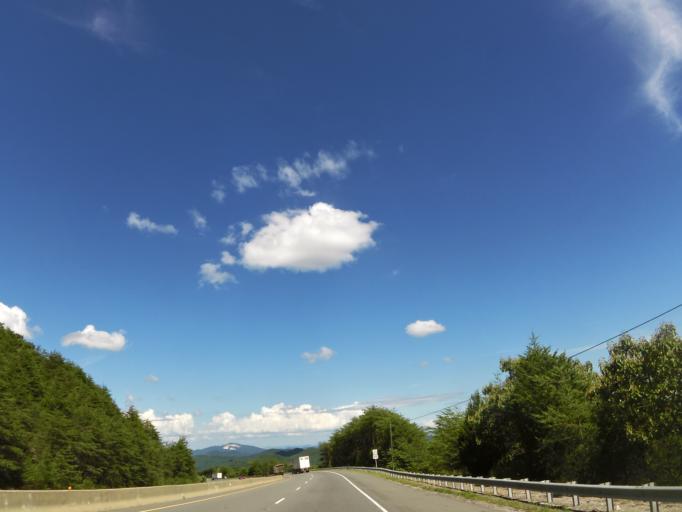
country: US
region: Tennessee
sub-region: Grainger County
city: Bean Station
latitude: 36.3508
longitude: -83.3908
